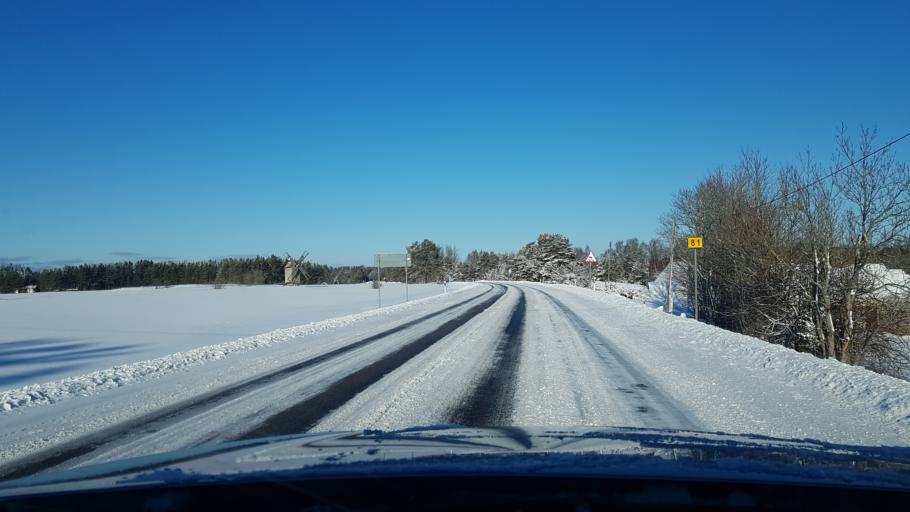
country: EE
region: Hiiumaa
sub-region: Kaerdla linn
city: Kardla
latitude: 58.9560
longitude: 22.7733
